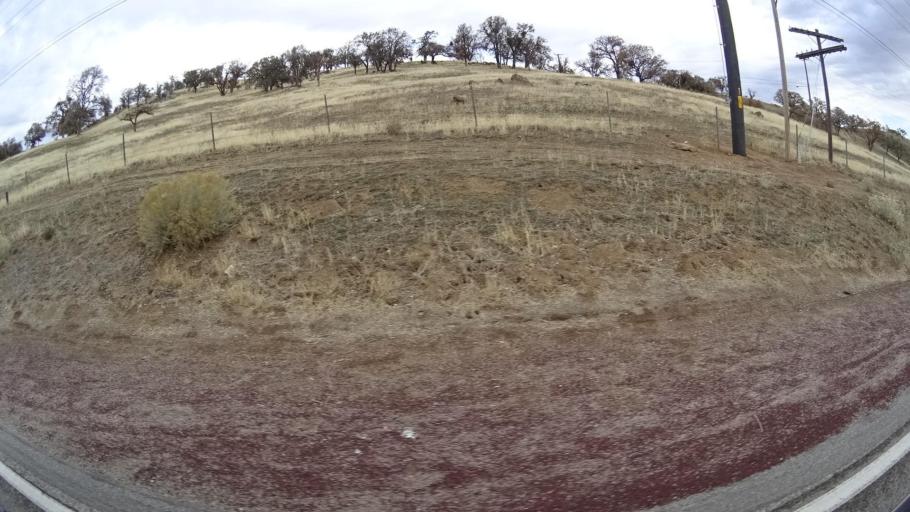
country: US
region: California
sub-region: Kern County
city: Golden Hills
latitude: 35.1129
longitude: -118.5222
